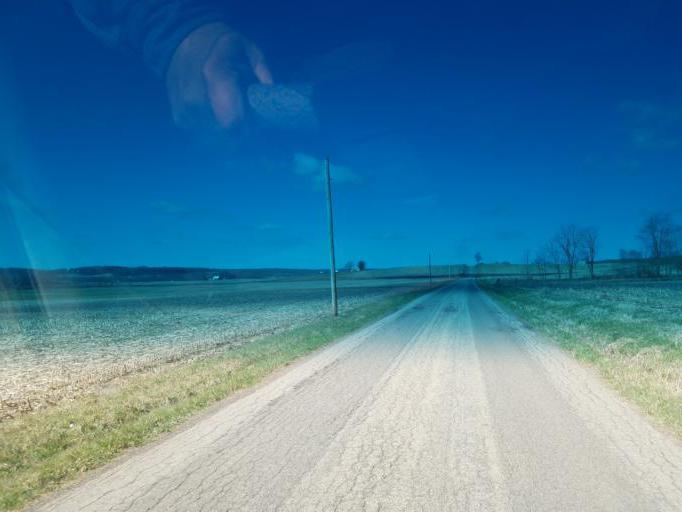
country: US
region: Ohio
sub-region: Knox County
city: Oak Hill
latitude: 40.2985
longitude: -82.2701
